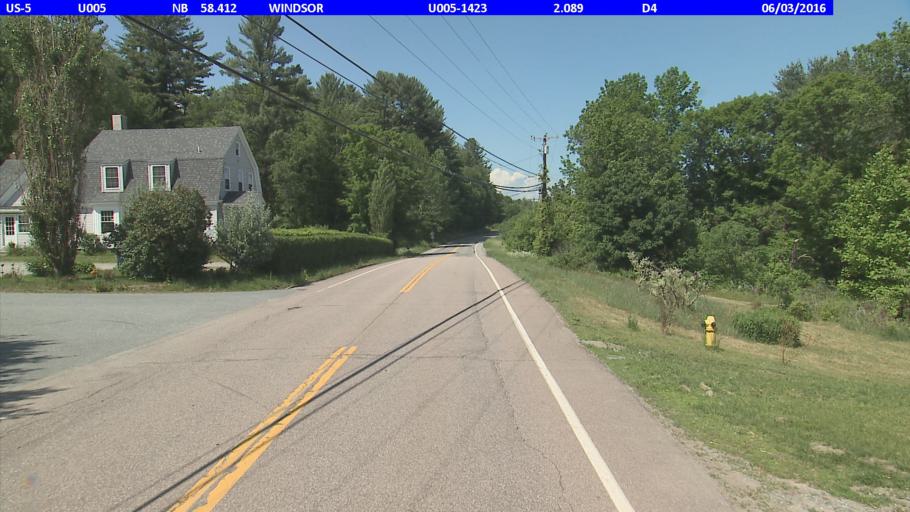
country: US
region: Vermont
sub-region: Windsor County
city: Windsor
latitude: 43.4583
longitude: -72.3941
